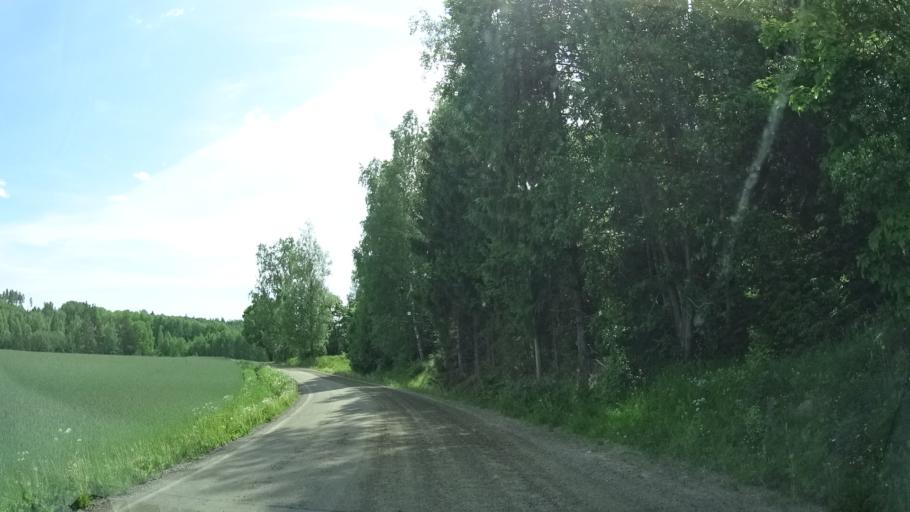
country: FI
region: Uusimaa
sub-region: Helsinki
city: Siuntio
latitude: 60.2063
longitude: 24.2624
